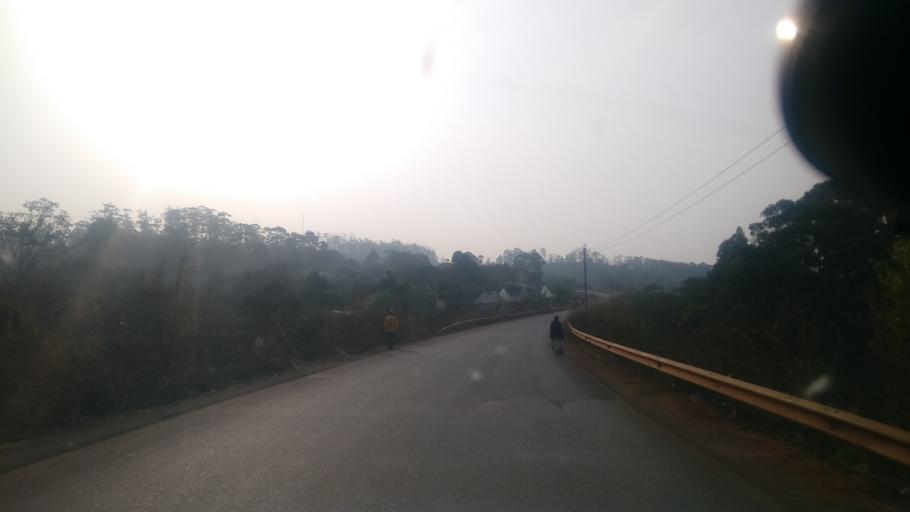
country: CM
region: West
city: Bangangte
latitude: 5.1587
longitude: 10.4925
